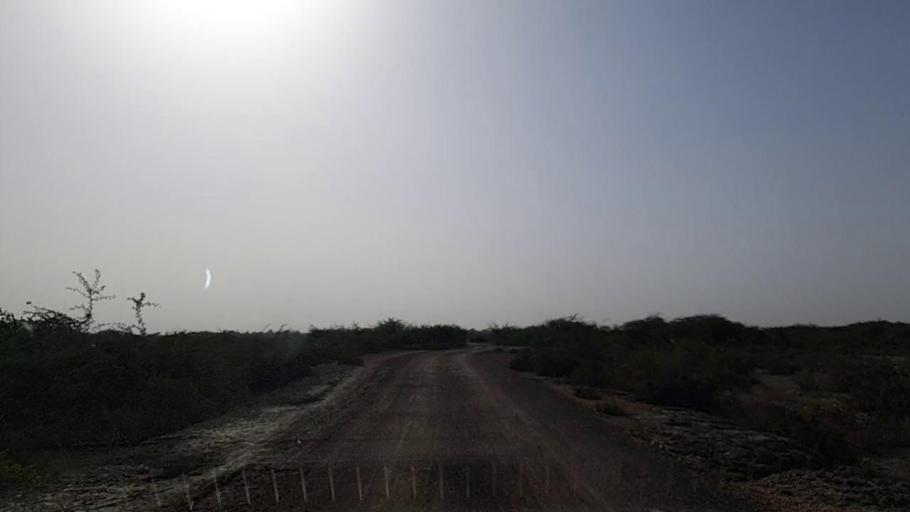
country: PK
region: Sindh
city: Jati
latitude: 24.2857
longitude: 68.2157
